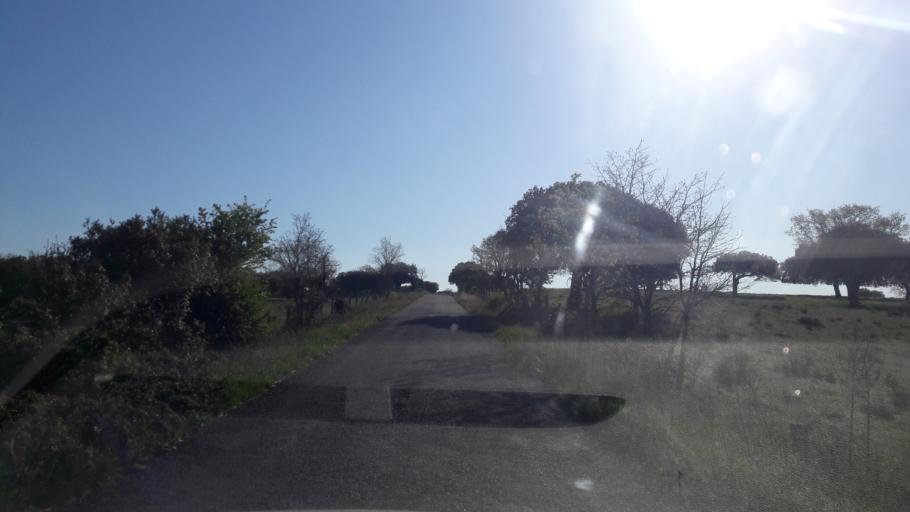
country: ES
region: Castille and Leon
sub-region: Provincia de Salamanca
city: Monleon
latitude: 40.6072
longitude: -5.8337
